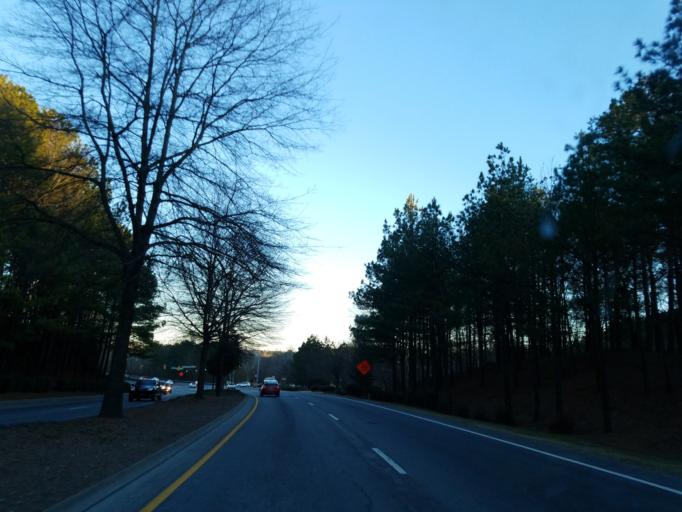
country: US
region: Georgia
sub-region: Cherokee County
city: Woodstock
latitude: 34.1028
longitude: -84.5382
